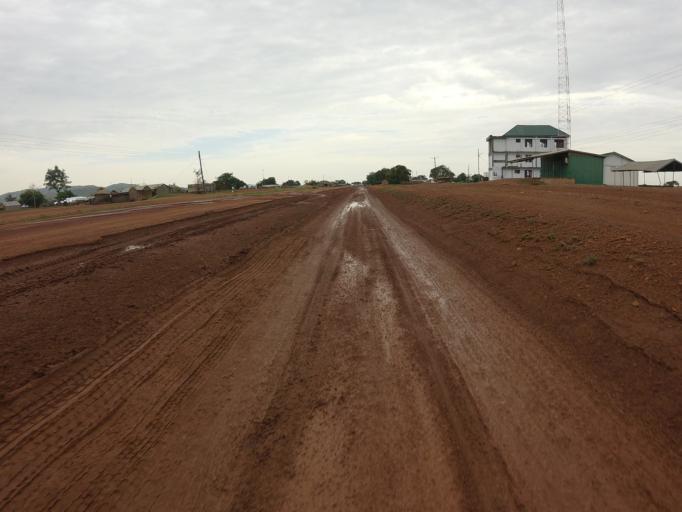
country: GH
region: Upper East
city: Bawku
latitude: 10.9293
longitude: -0.5032
